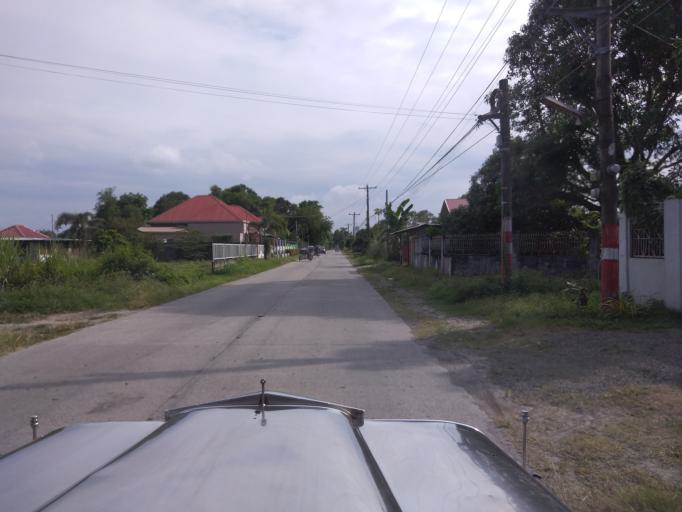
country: PH
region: Central Luzon
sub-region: Province of Pampanga
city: San Patricio
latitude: 15.1007
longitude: 120.7090
